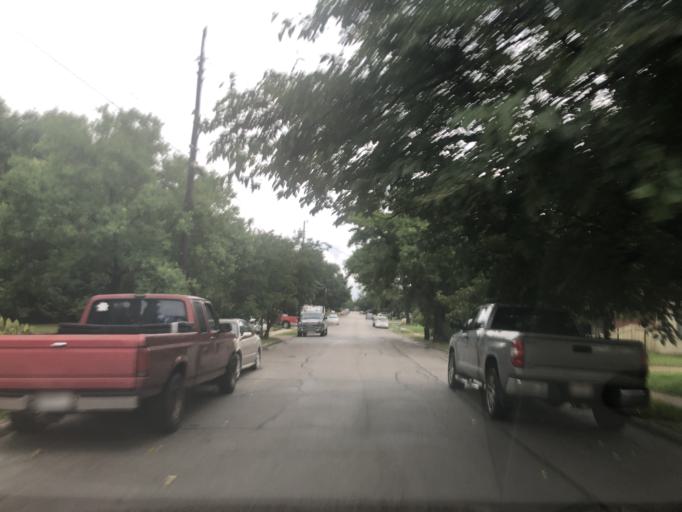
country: US
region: Texas
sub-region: Dallas County
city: Irving
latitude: 32.7969
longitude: -96.9507
